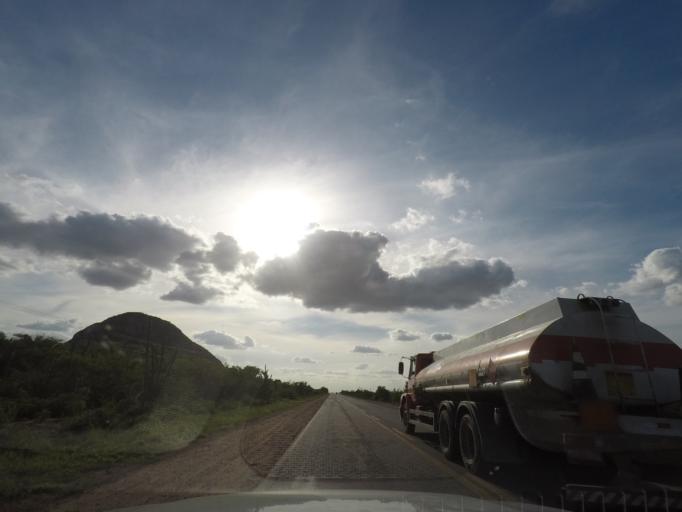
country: BR
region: Bahia
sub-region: Anguera
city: Anguera
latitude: -12.1820
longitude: -39.4601
